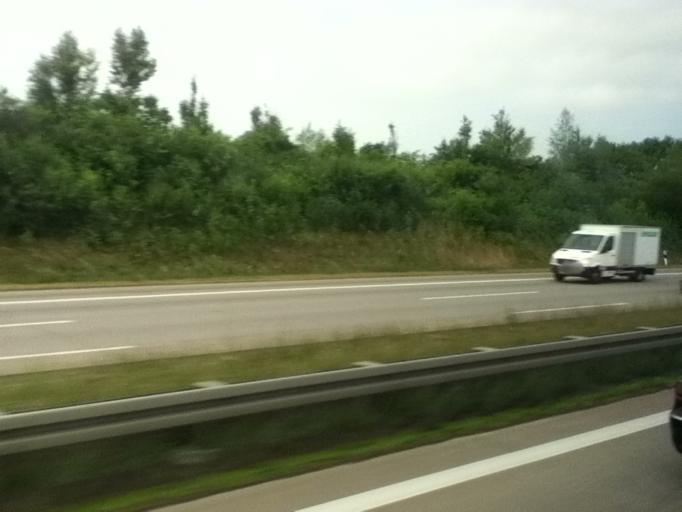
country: DE
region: Saxony
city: Wilsdruff
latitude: 51.0600
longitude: 13.4955
